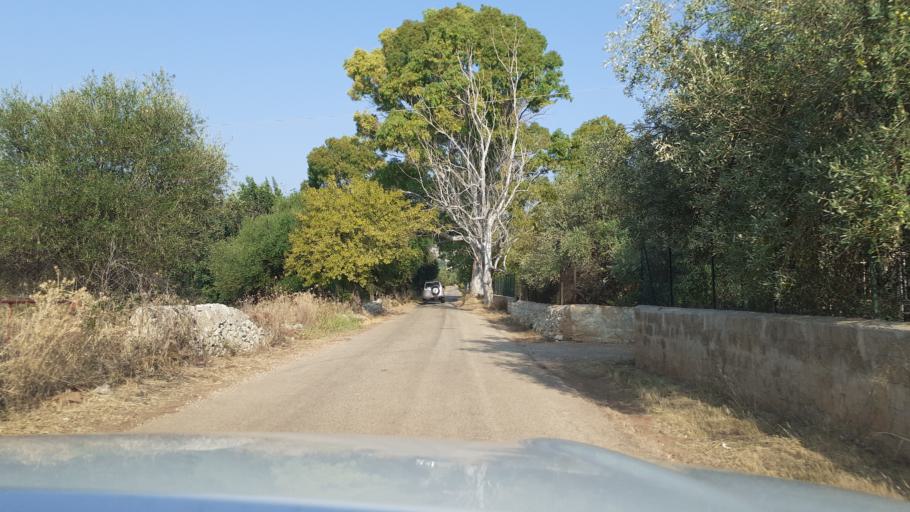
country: IT
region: Sicily
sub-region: Provincia di Siracusa
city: Cassibile
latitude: 36.9753
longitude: 15.1852
